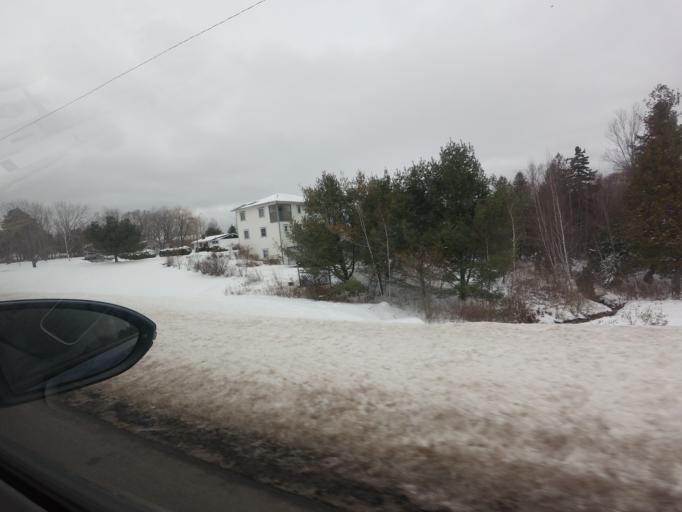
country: CA
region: New Brunswick
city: Oromocto
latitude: 45.8458
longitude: -66.5032
